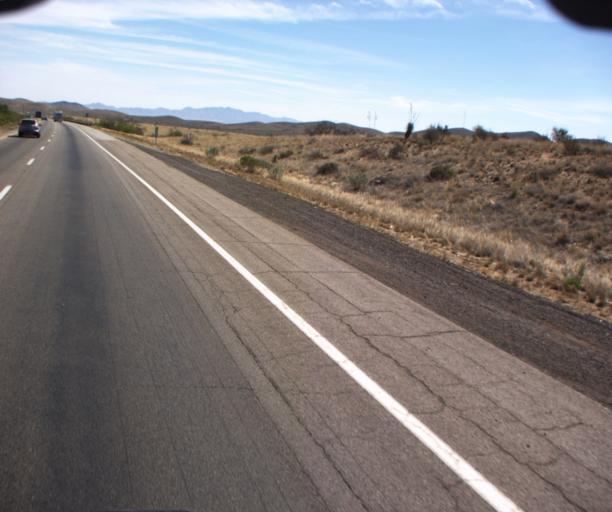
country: US
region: Arizona
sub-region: Cochise County
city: Saint David
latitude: 32.0841
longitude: -110.0466
